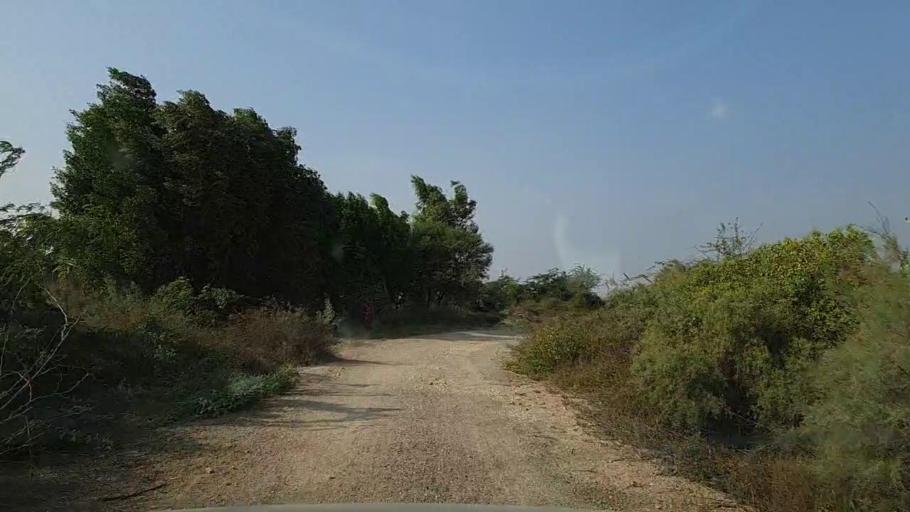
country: PK
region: Sindh
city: Mirpur Sakro
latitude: 24.5796
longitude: 67.5679
